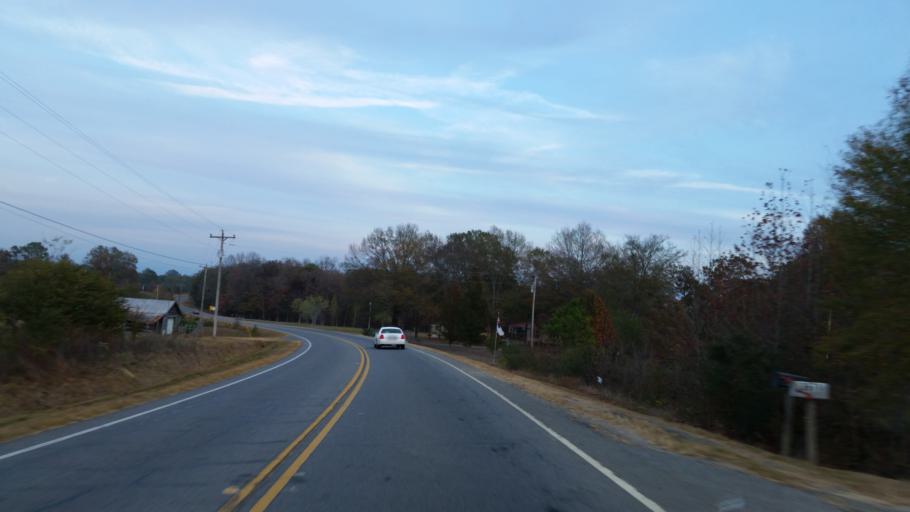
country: US
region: Georgia
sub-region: Gordon County
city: Calhoun
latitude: 34.6014
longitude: -84.8403
